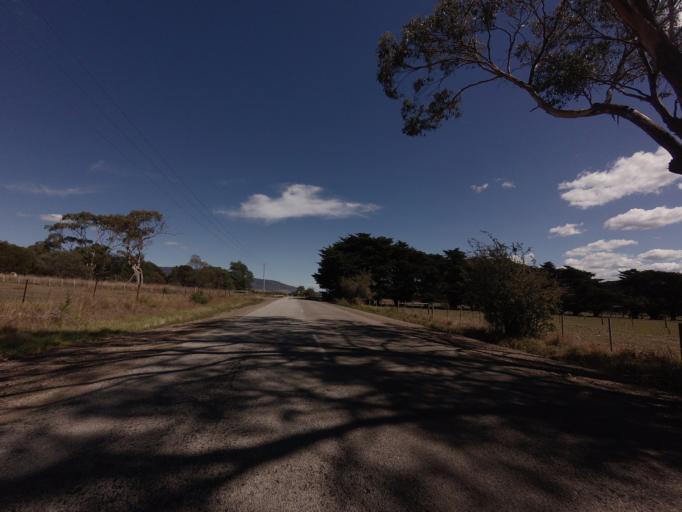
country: AU
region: Tasmania
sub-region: Break O'Day
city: St Helens
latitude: -41.6174
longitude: 148.0074
